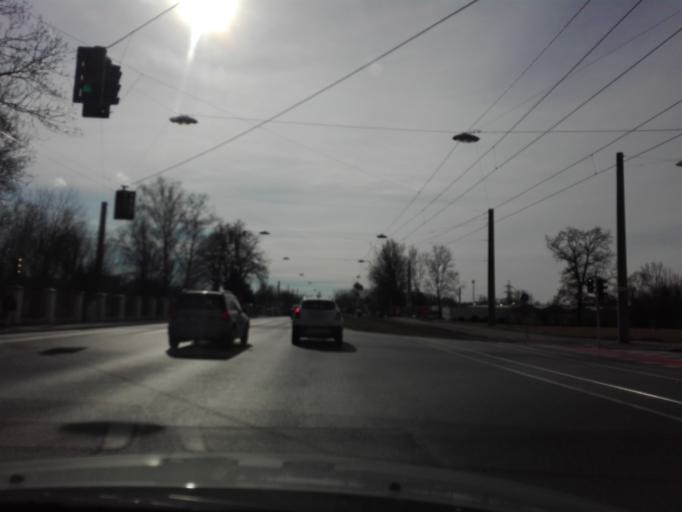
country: AT
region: Upper Austria
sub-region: Politischer Bezirk Linz-Land
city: Ansfelden
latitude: 48.2536
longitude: 14.3228
